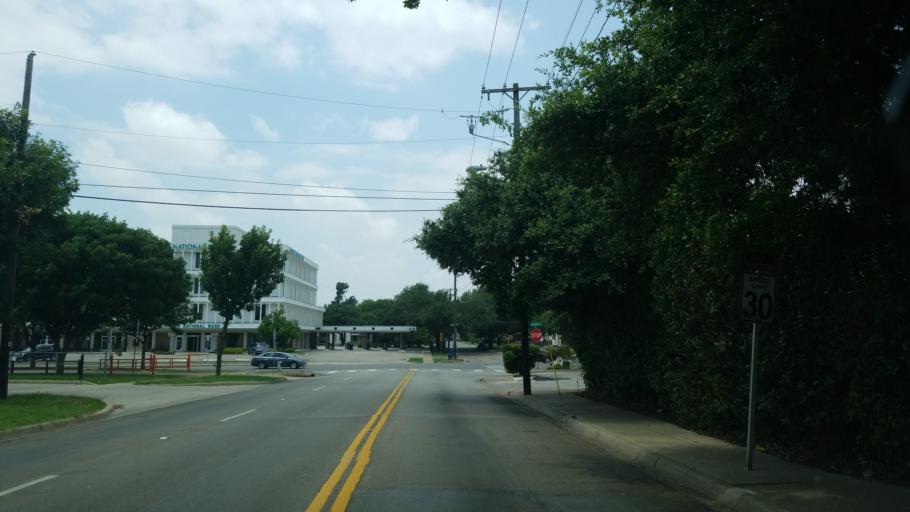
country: US
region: Texas
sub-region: Dallas County
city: University Park
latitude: 32.8493
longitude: -96.8205
